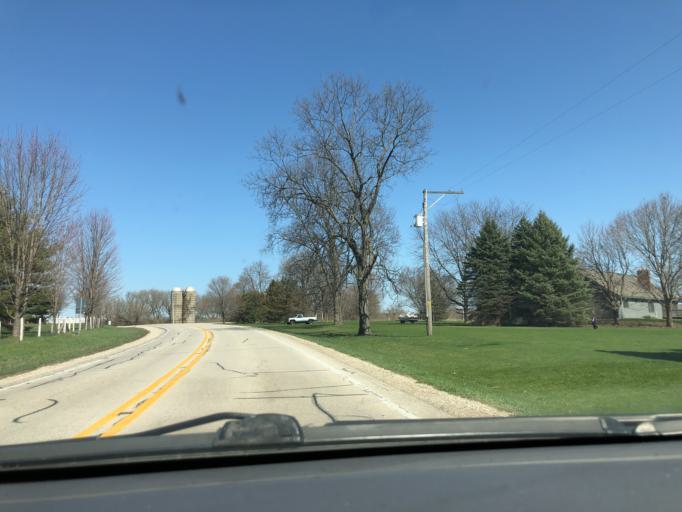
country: US
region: Illinois
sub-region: McHenry County
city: Huntley
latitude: 42.1610
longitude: -88.4838
